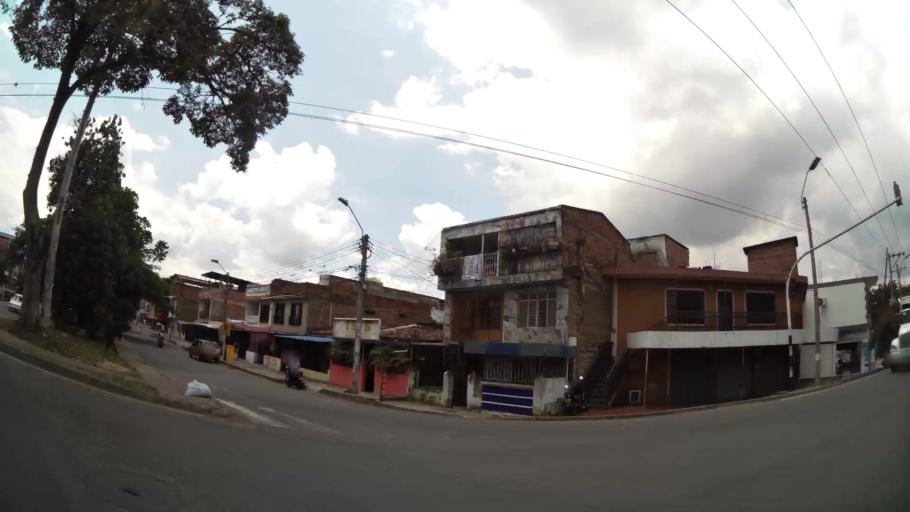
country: CO
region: Valle del Cauca
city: Cali
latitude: 3.4644
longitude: -76.4801
